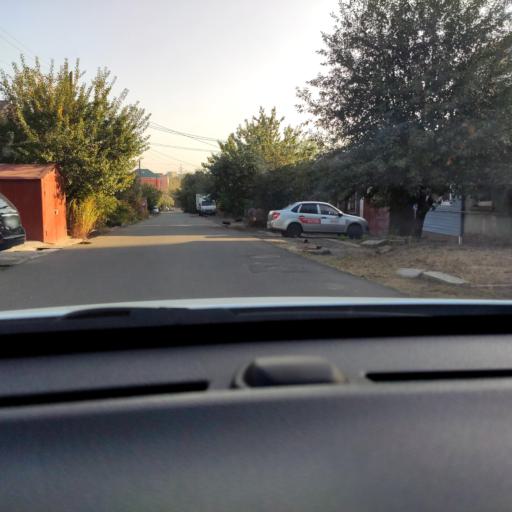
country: RU
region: Voronezj
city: Voronezh
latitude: 51.6927
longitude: 39.1504
